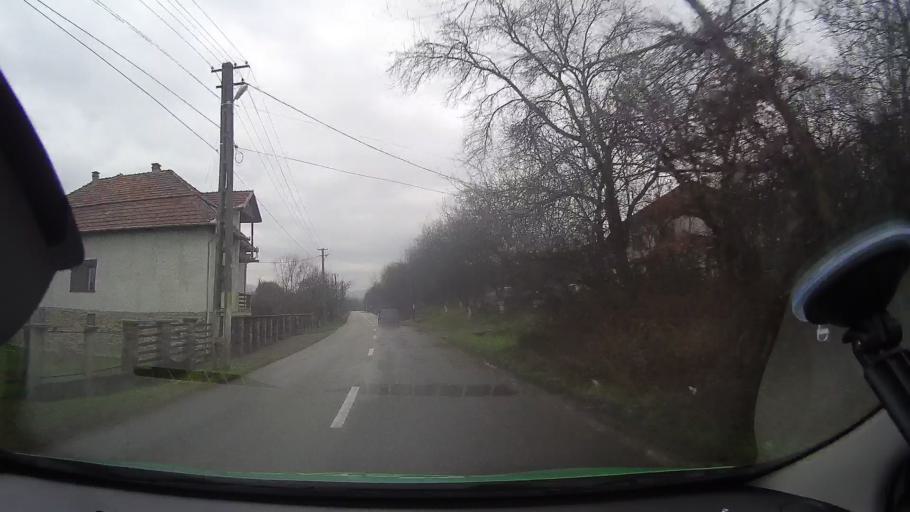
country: RO
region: Arad
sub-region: Comuna Gurahont
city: Gurahont
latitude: 46.2639
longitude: 22.3410
